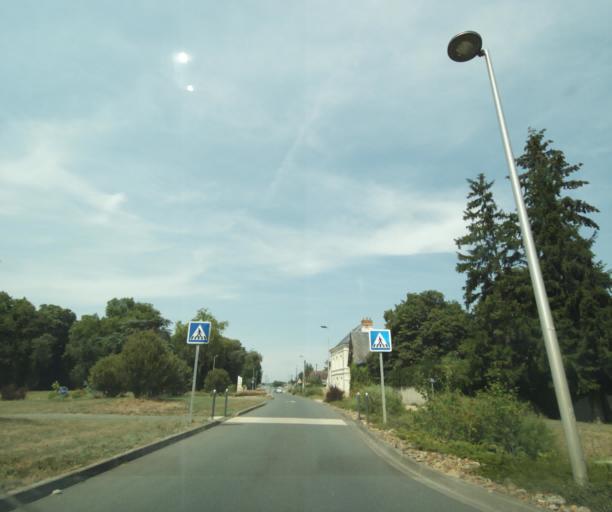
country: FR
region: Poitou-Charentes
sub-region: Departement de la Vienne
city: Antran
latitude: 46.8817
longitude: 0.5675
